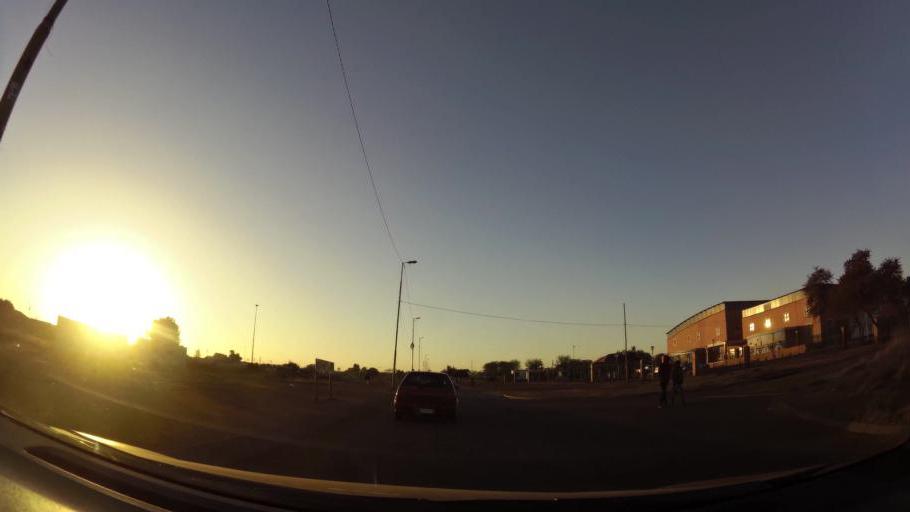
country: ZA
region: Gauteng
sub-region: City of Tshwane Metropolitan Municipality
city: Mabopane
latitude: -25.5849
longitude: 28.0889
